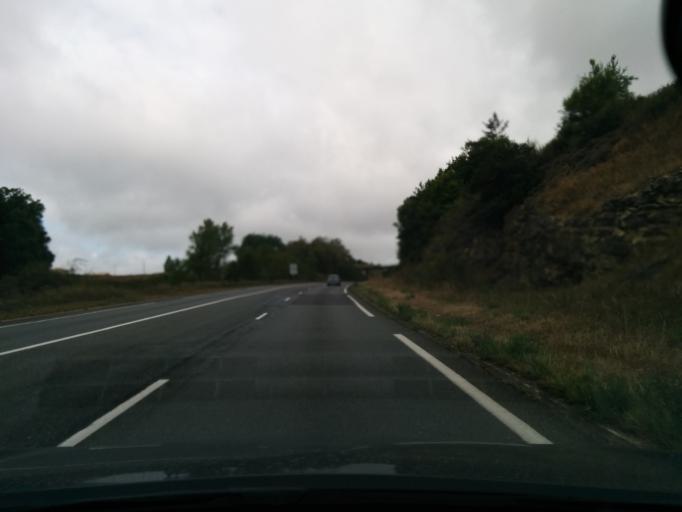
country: FR
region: Midi-Pyrenees
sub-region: Departement du Lot
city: Cahors
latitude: 44.4345
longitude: 1.4264
